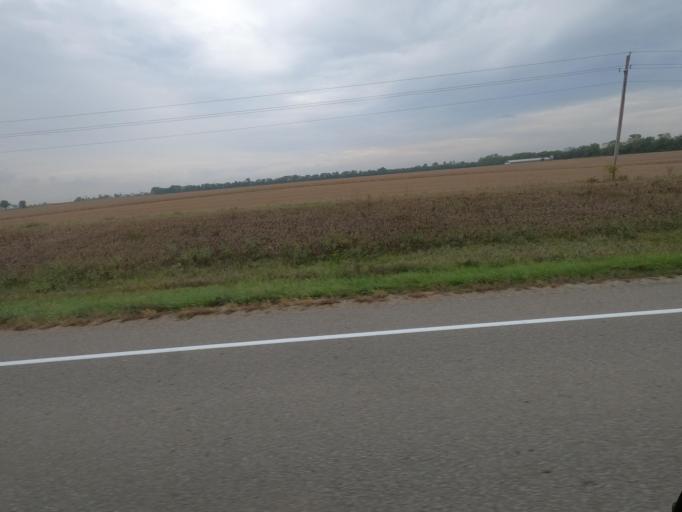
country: US
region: Iowa
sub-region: Van Buren County
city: Keosauqua
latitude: 40.8133
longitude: -91.7704
